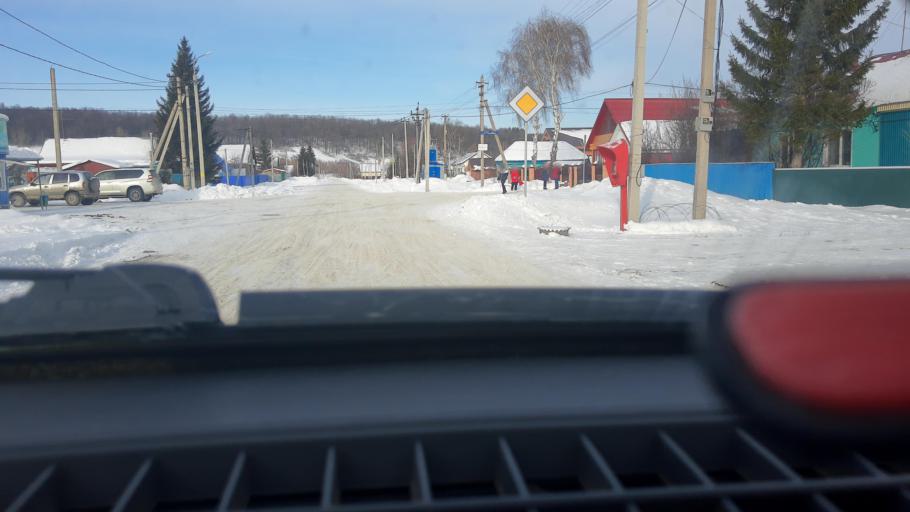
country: RU
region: Bashkortostan
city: Ufa
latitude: 54.5198
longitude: 55.9119
